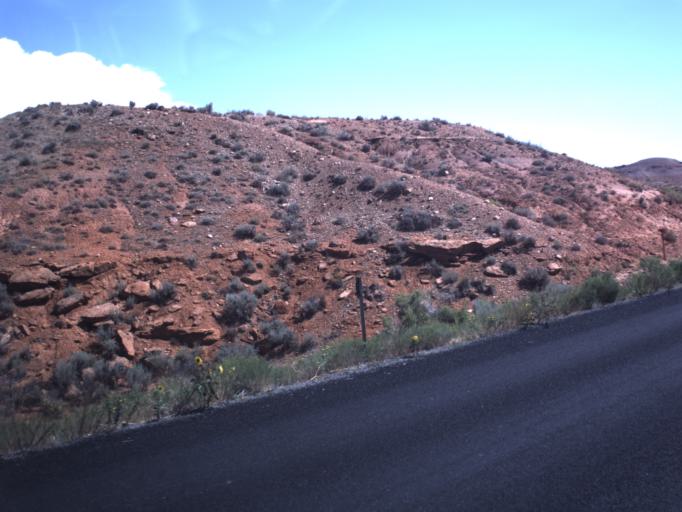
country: US
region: Utah
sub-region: Uintah County
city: Maeser
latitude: 40.4118
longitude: -109.7324
